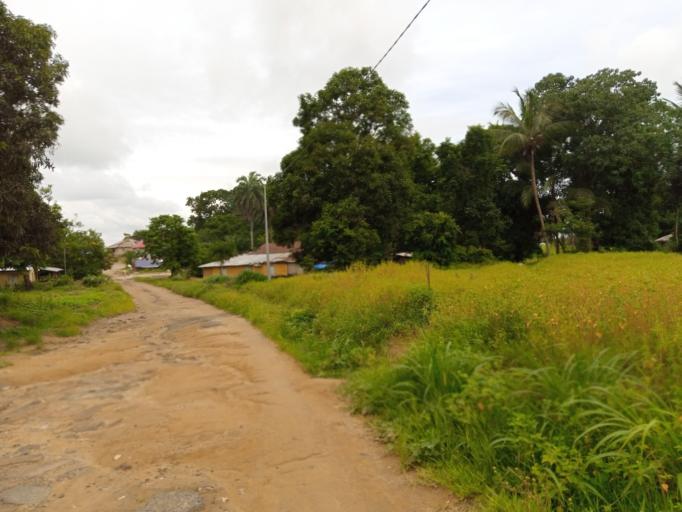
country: SL
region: Northern Province
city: Masoyila
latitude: 8.5955
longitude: -13.2006
